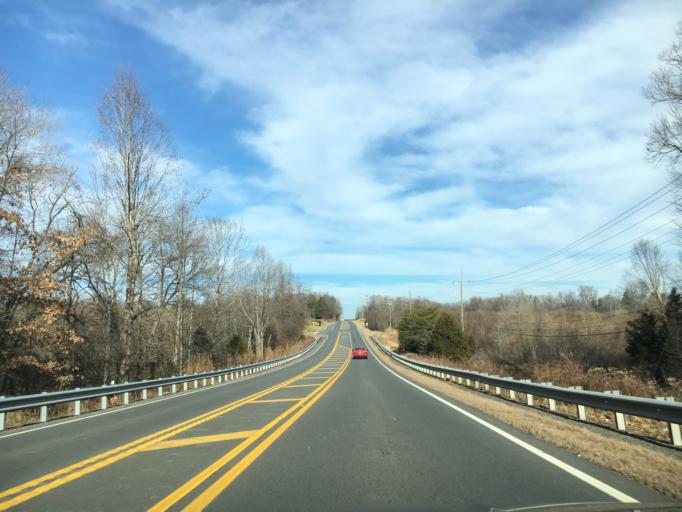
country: US
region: Virginia
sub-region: Fauquier County
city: Warrenton
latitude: 38.6588
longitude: -77.9250
